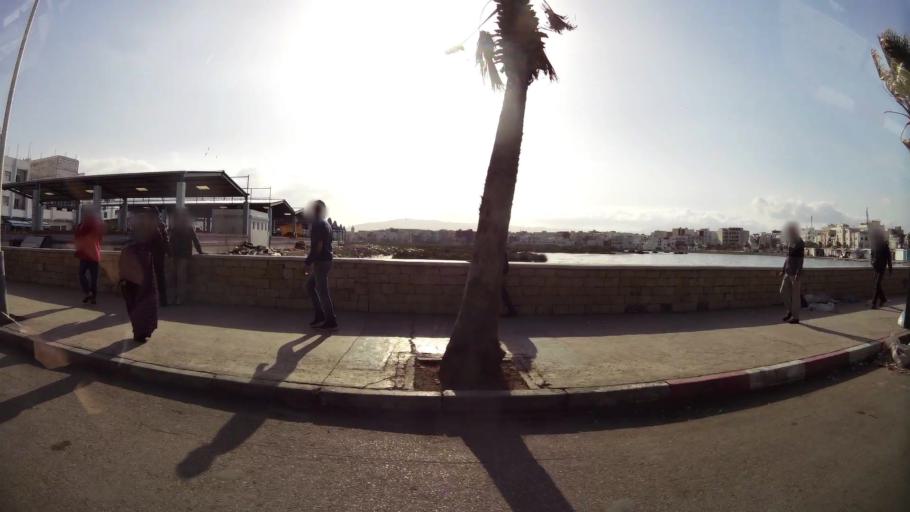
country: MA
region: Tanger-Tetouan
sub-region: Tetouan
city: Martil
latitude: 35.6136
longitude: -5.2735
